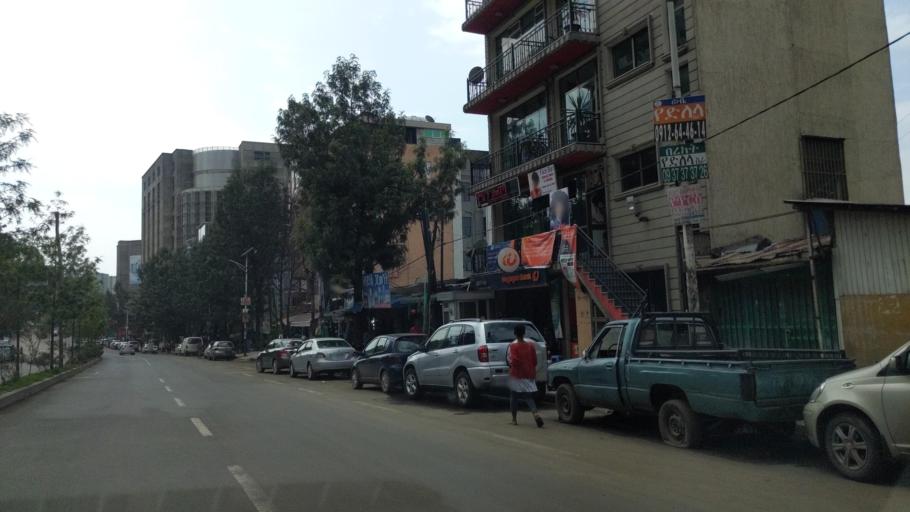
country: ET
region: Adis Abeba
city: Addis Ababa
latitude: 9.0036
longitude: 38.7972
